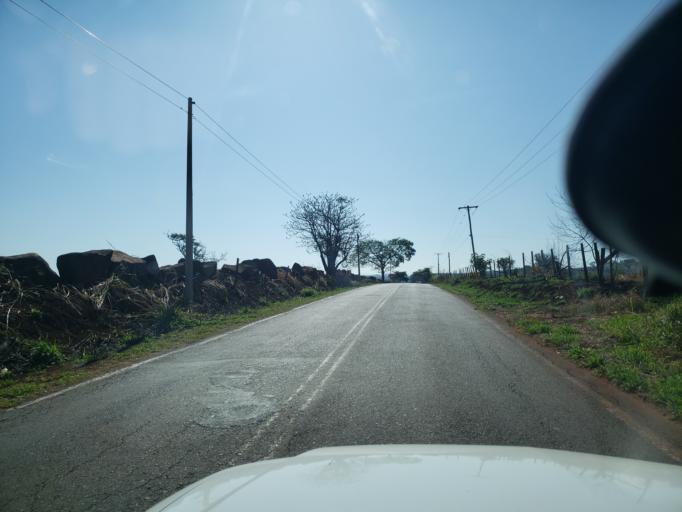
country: BR
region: Sao Paulo
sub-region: Moji-Guacu
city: Mogi-Gaucu
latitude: -22.3411
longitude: -46.8881
